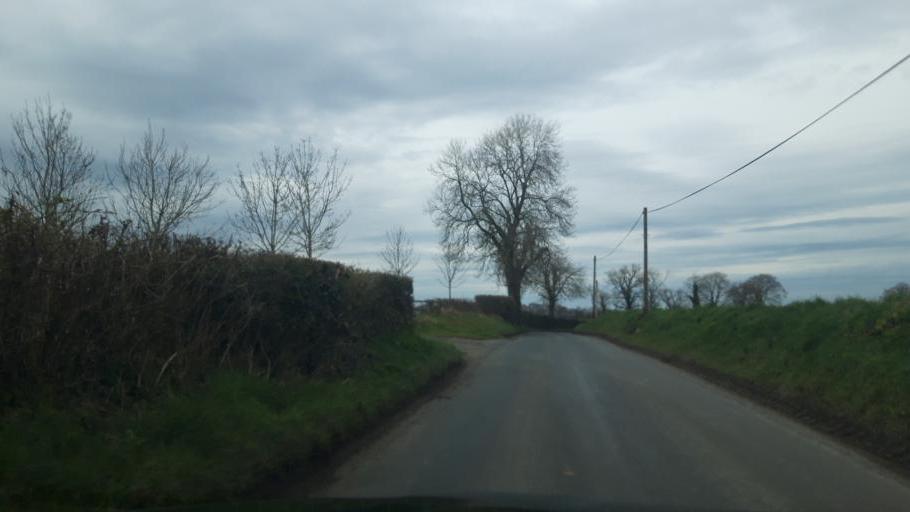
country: IE
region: Leinster
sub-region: Kildare
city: Rathangan
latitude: 53.2466
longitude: -6.9567
